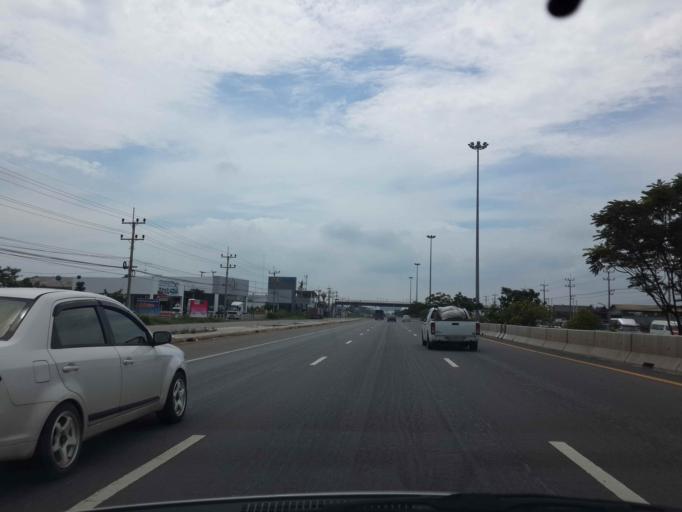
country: TH
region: Samut Songkhram
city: Samut Songkhram
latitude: 13.4194
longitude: 100.0324
